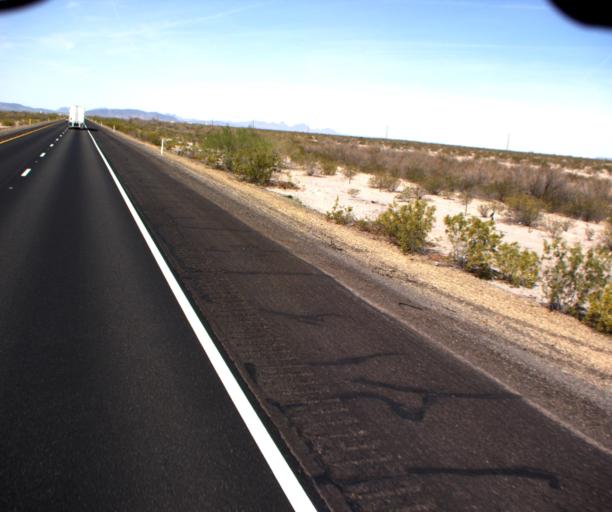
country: US
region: Arizona
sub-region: La Paz County
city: Salome
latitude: 33.6221
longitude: -113.7054
